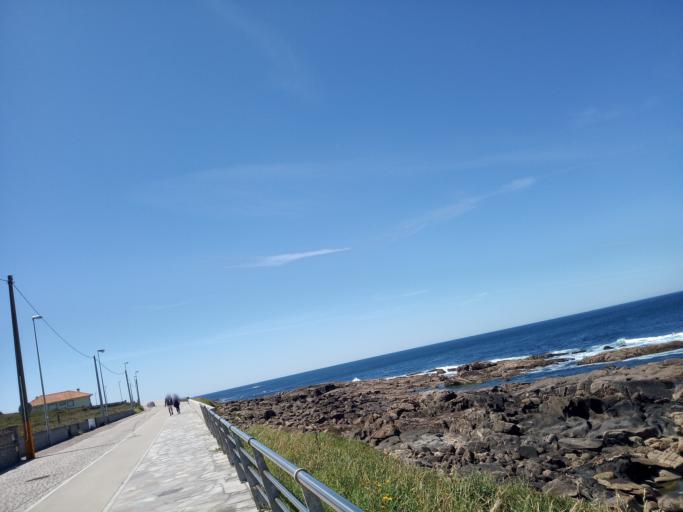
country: ES
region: Galicia
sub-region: Provincia de Pontevedra
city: A Guarda
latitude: 41.8928
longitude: -8.8797
